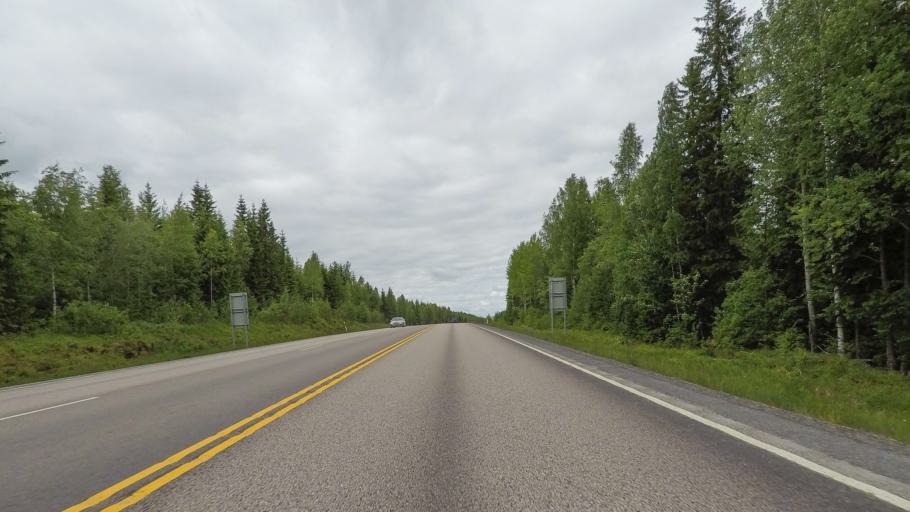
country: FI
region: Central Finland
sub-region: Jyvaeskylae
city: Toivakka
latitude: 62.0341
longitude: 26.0486
